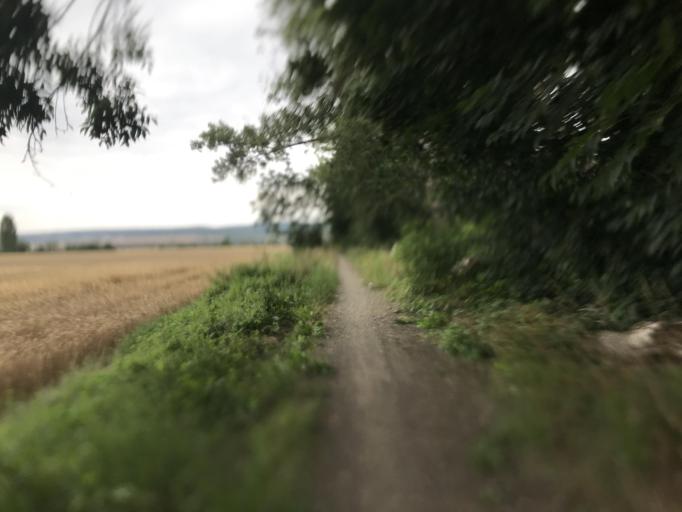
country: DE
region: Saxony-Anhalt
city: Weddersleben
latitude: 51.7686
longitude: 11.1051
